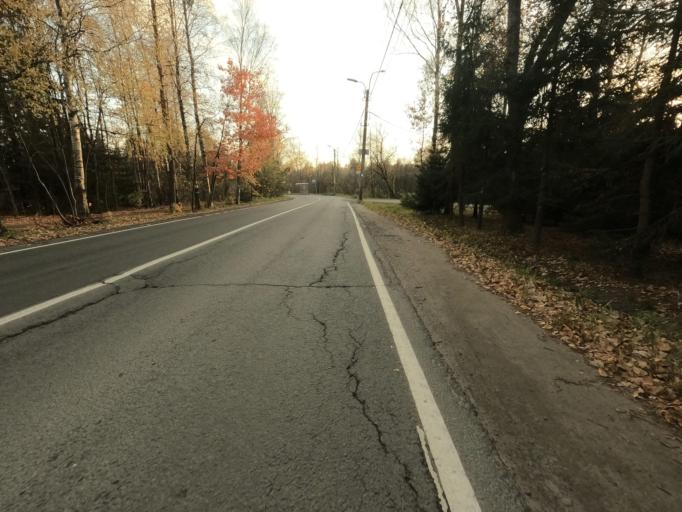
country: RU
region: St.-Petersburg
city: Beloostrov
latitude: 60.1607
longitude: 30.0060
